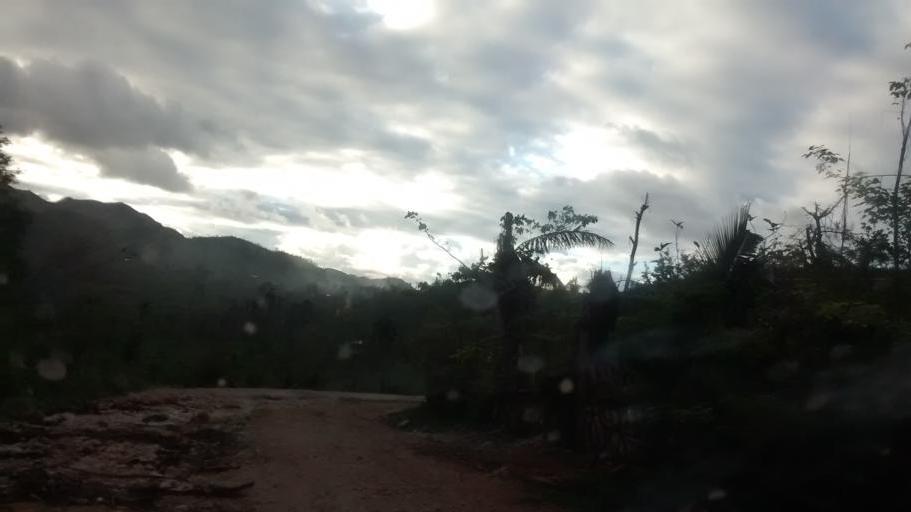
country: HT
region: Grandans
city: Corail
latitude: 18.4785
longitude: -73.8029
